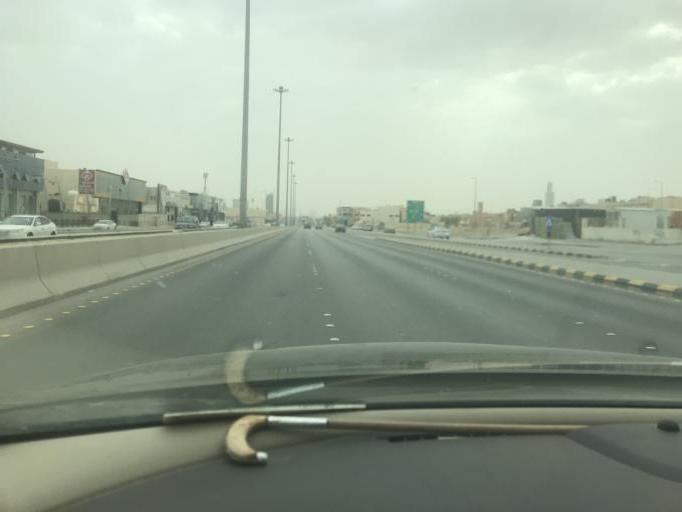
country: SA
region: Ar Riyad
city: Riyadh
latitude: 24.8219
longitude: 46.6501
